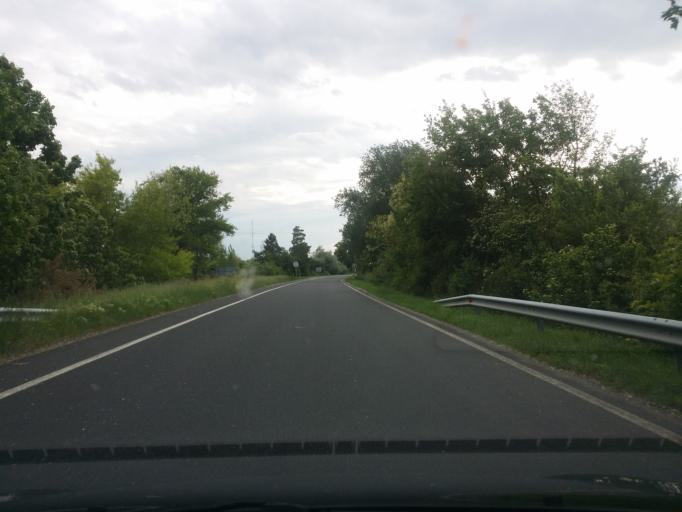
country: HU
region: Somogy
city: Balatonszabadi
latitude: 46.9305
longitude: 18.1334
